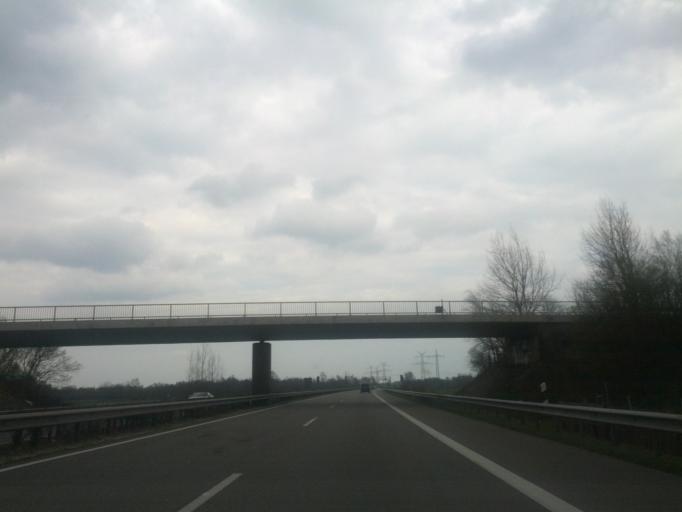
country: DE
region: Lower Saxony
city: Apen
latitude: 53.2692
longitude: 7.7820
